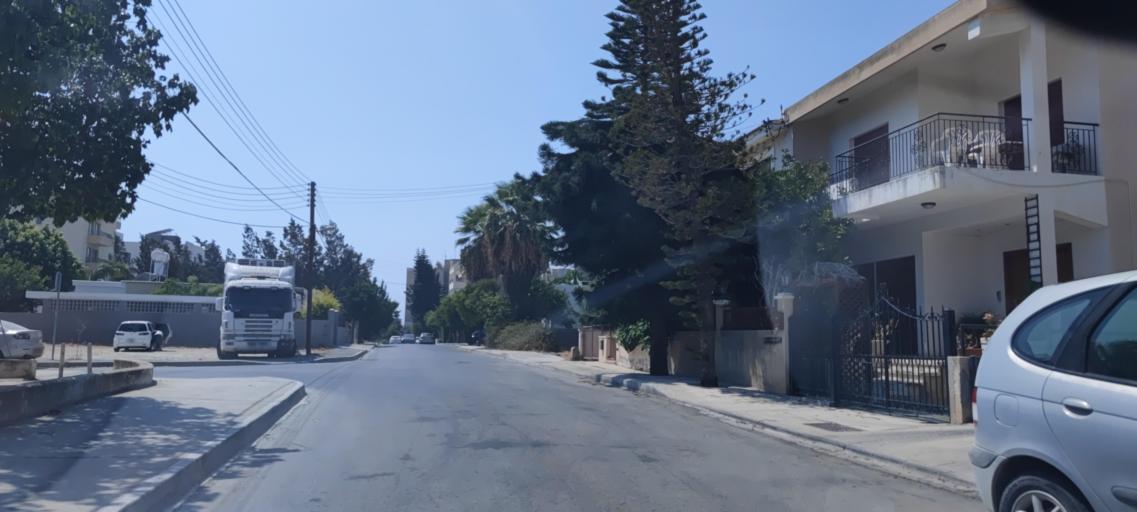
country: CY
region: Limassol
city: Limassol
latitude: 34.6789
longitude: 33.0316
